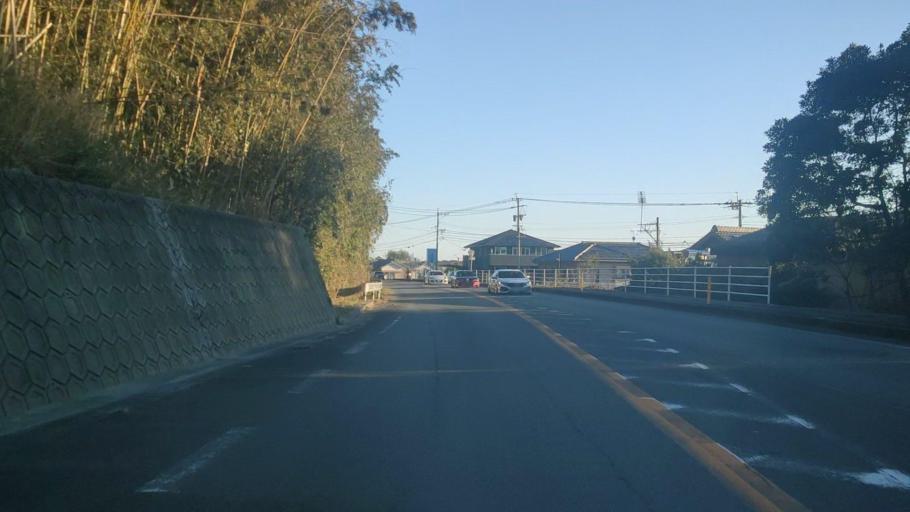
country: JP
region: Miyazaki
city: Takanabe
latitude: 32.0786
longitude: 131.5078
